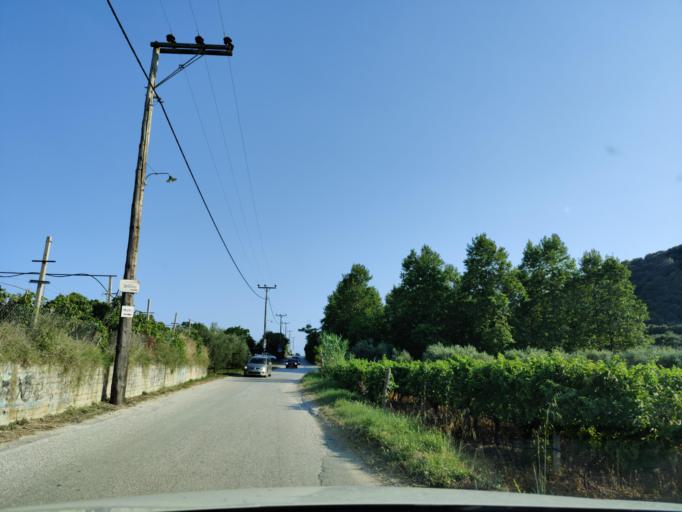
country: GR
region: East Macedonia and Thrace
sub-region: Nomos Kavalas
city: Nea Peramos
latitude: 40.8230
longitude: 24.3078
